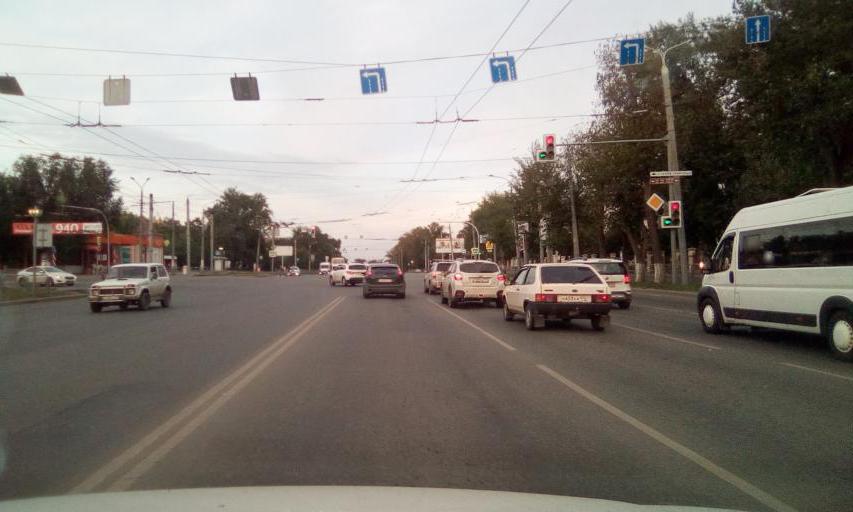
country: RU
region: Chelyabinsk
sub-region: Gorod Chelyabinsk
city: Chelyabinsk
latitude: 55.1603
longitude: 61.4502
